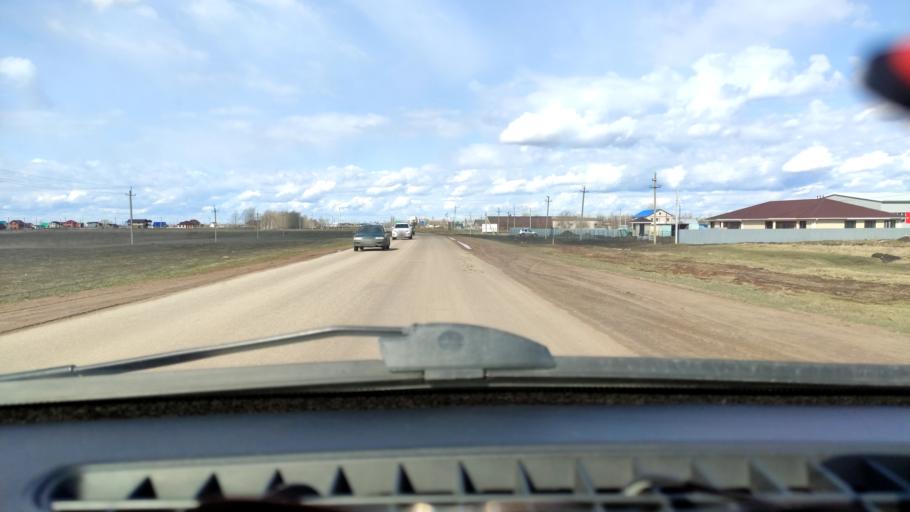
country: RU
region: Bashkortostan
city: Kabakovo
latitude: 54.5401
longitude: 56.1390
